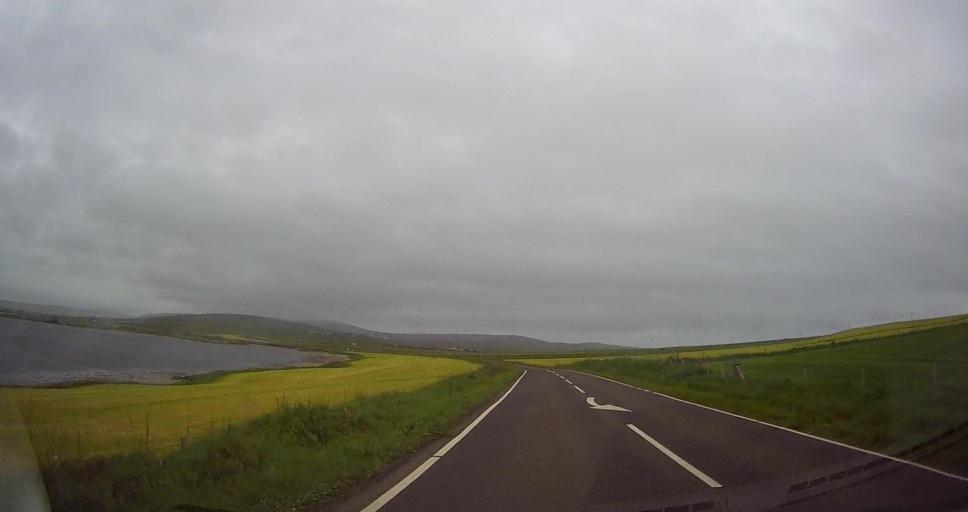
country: GB
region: Scotland
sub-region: Orkney Islands
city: Stromness
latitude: 58.9862
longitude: -3.2667
